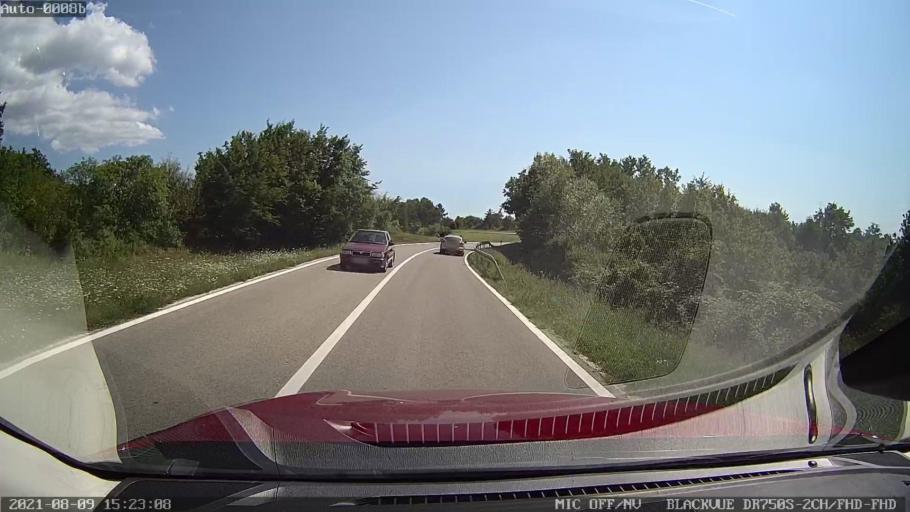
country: HR
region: Istarska
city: Pazin
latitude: 45.1851
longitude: 13.9029
